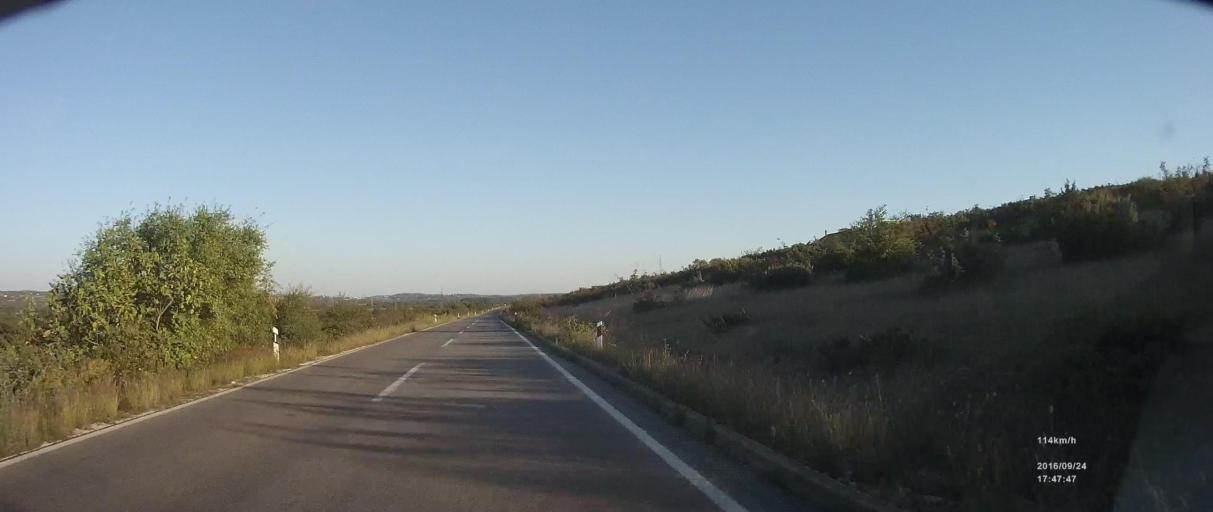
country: HR
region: Zadarska
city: Polaca
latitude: 44.0711
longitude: 15.5282
